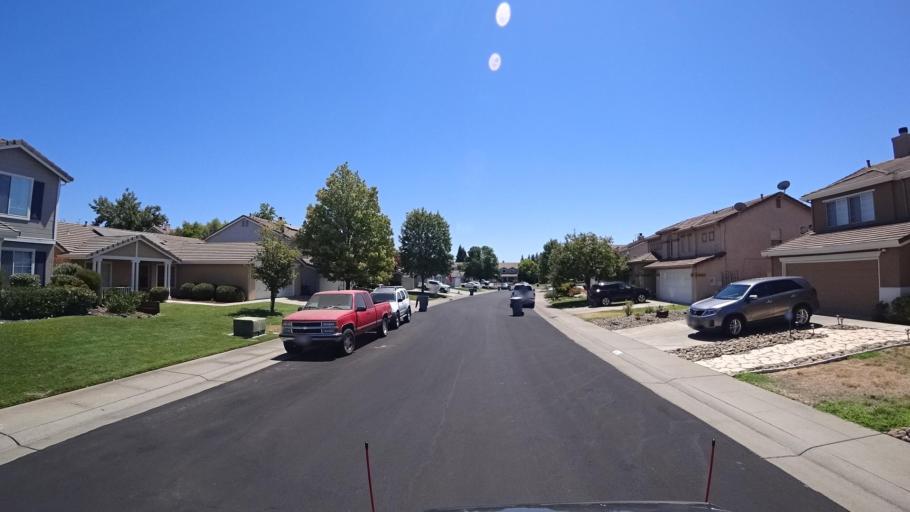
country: US
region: California
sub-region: Placer County
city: Rocklin
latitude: 38.8169
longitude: -121.2734
